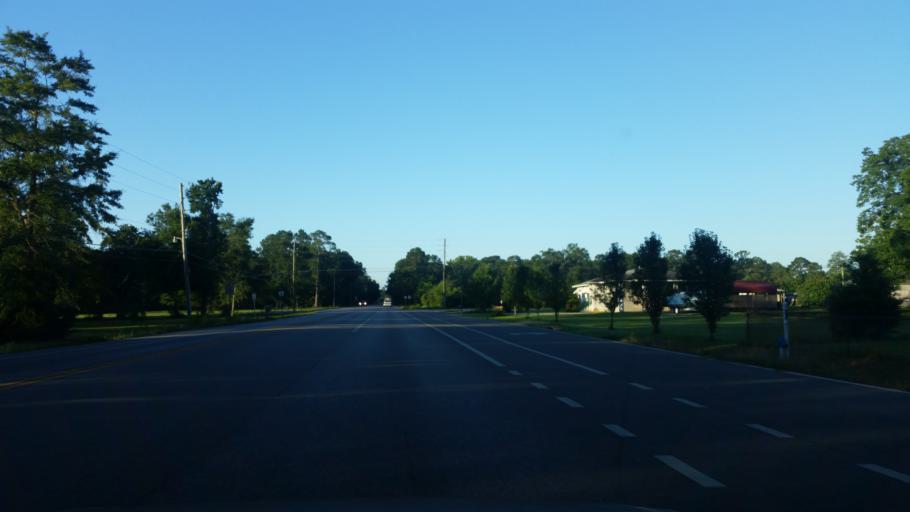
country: US
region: Florida
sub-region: Escambia County
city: Cantonment
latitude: 30.5797
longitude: -87.3496
